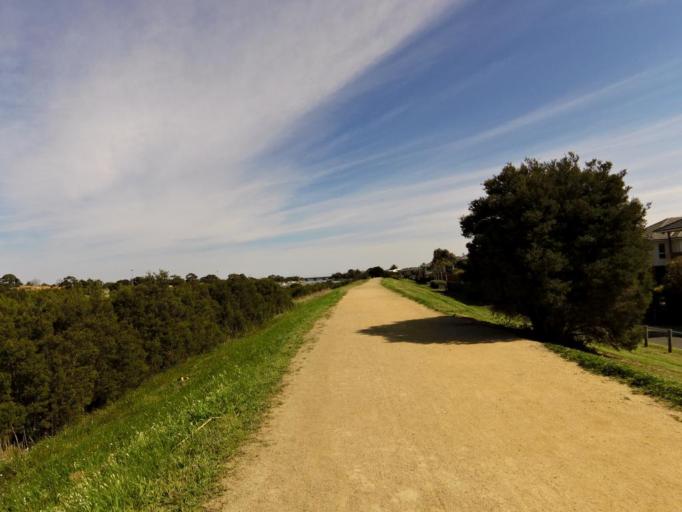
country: AU
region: Victoria
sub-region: Kingston
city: Patterson Lakes
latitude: -38.0684
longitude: 145.1338
